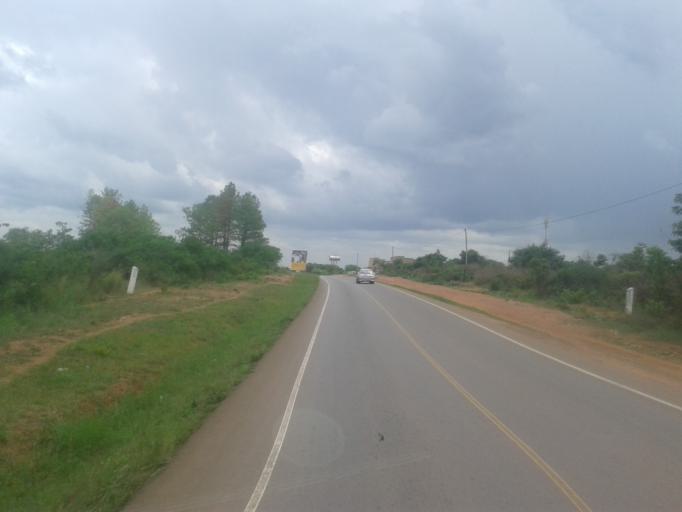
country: UG
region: Central Region
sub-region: Nakasongola District
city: Nakasongola
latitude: 1.2413
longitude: 32.4625
